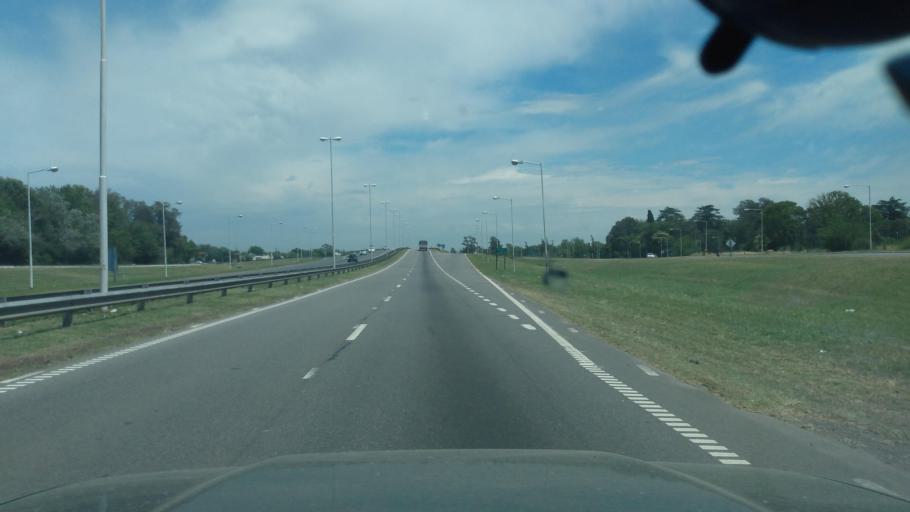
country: AR
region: Buenos Aires
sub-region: Partido de Lujan
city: Lujan
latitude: -34.5577
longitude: -59.0965
